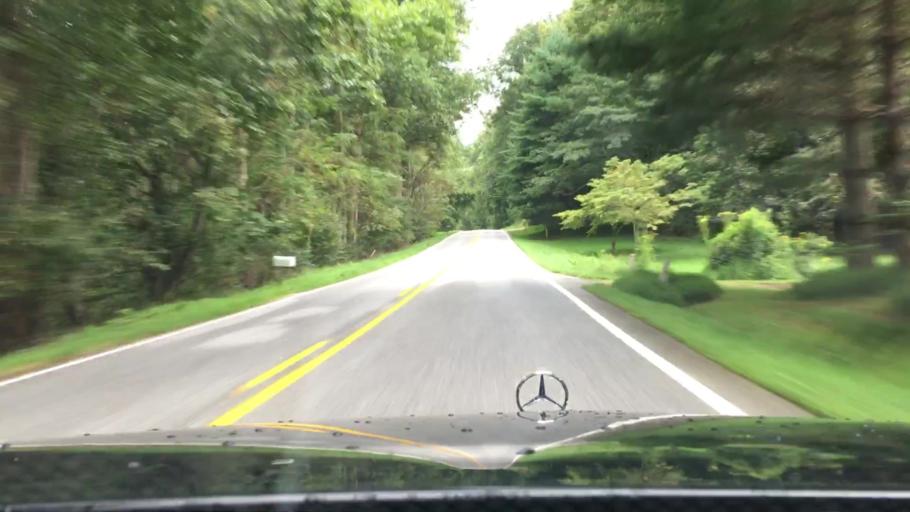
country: US
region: Virginia
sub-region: Nelson County
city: Nellysford
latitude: 37.8323
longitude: -78.9319
